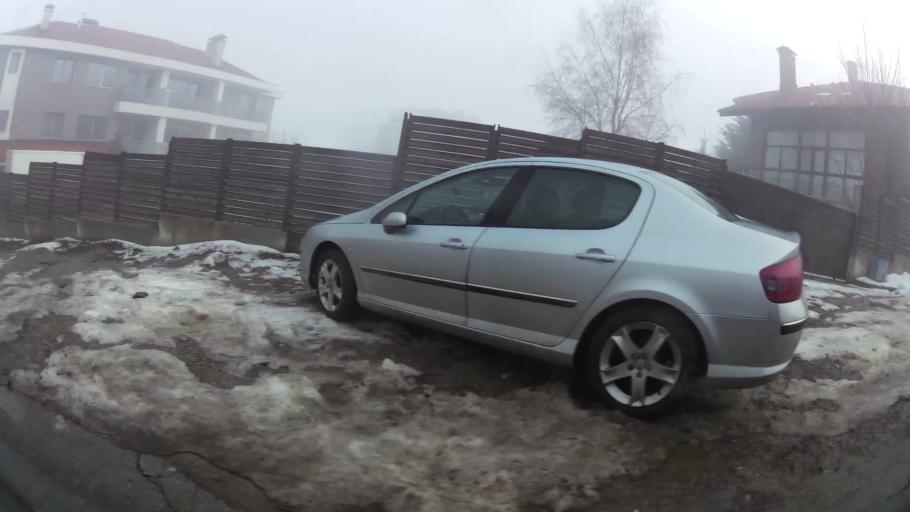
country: BG
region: Sofia-Capital
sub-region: Stolichna Obshtina
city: Sofia
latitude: 42.6553
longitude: 23.2554
